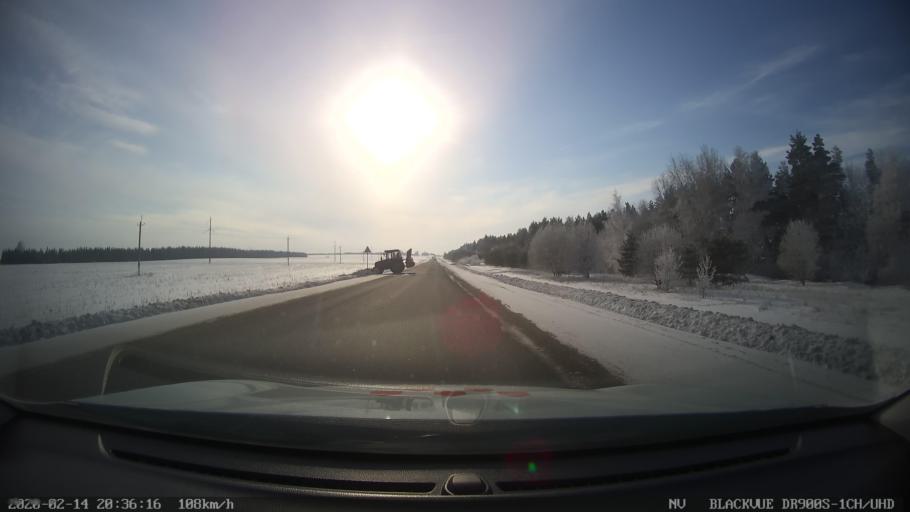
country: RU
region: Tatarstan
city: Kuybyshevskiy Zaton
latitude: 55.3702
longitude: 48.9985
